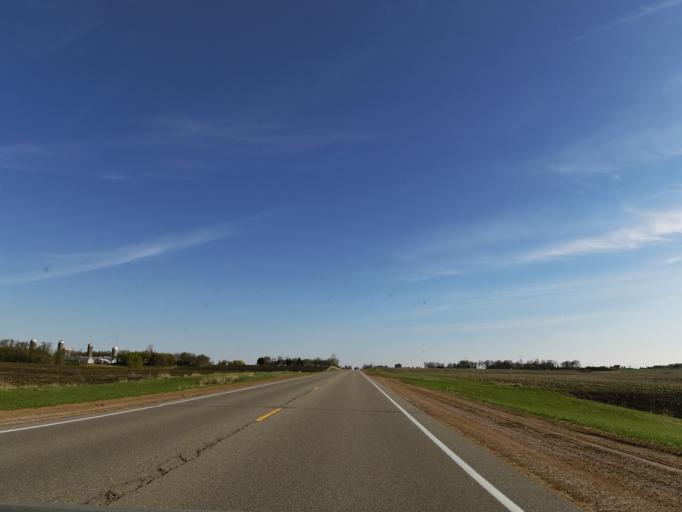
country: US
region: Minnesota
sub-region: Le Sueur County
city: New Prague
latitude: 44.6097
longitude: -93.5014
